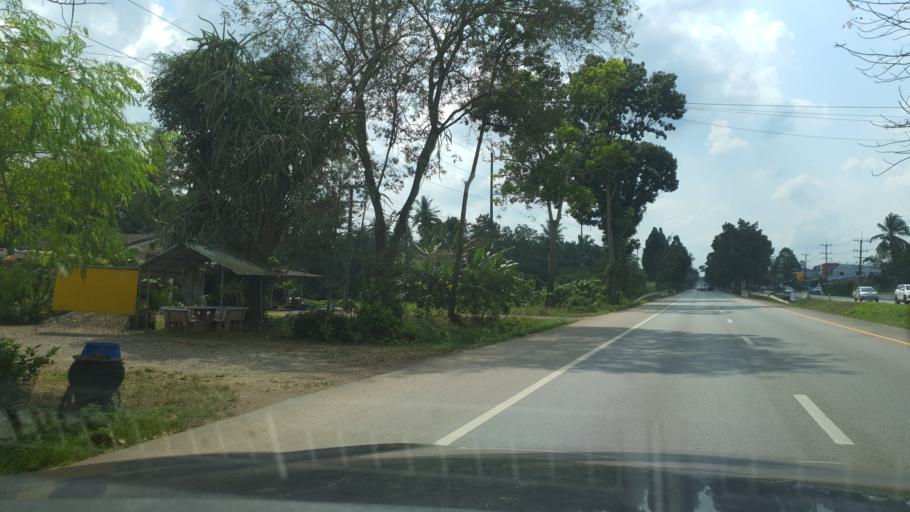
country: TH
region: Chumphon
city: Tha Sae
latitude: 10.6838
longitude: 99.2041
